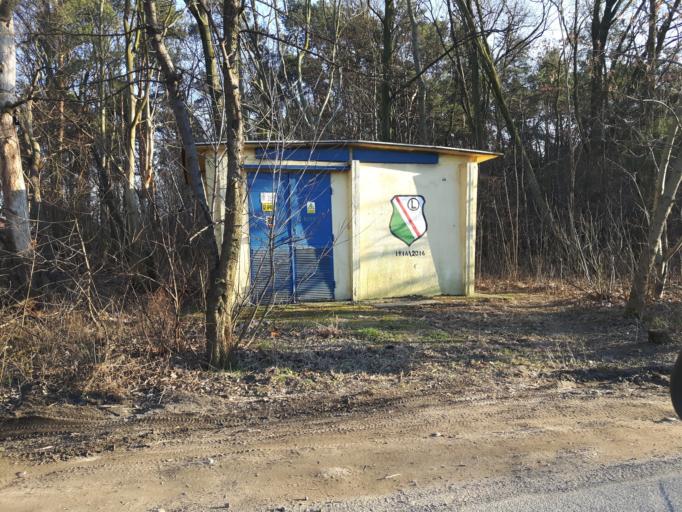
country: PL
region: Masovian Voivodeship
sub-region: Powiat wolominski
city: Marki
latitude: 52.3183
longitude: 21.0986
